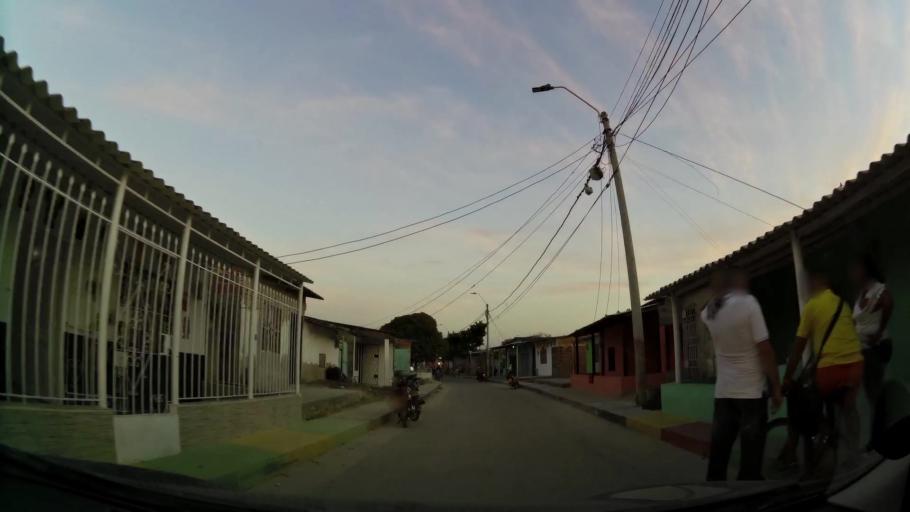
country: CO
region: Atlantico
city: Barranquilla
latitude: 10.9527
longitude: -74.8316
